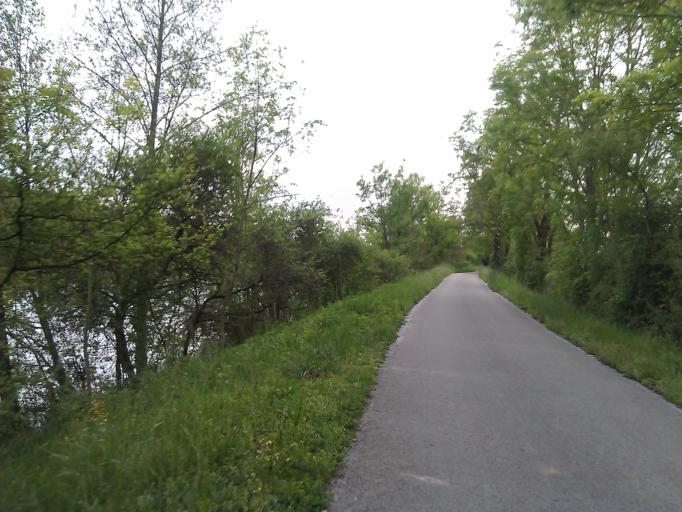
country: FR
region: Franche-Comte
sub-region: Departement du Jura
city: Fraisans
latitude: 47.1633
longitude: 5.7775
